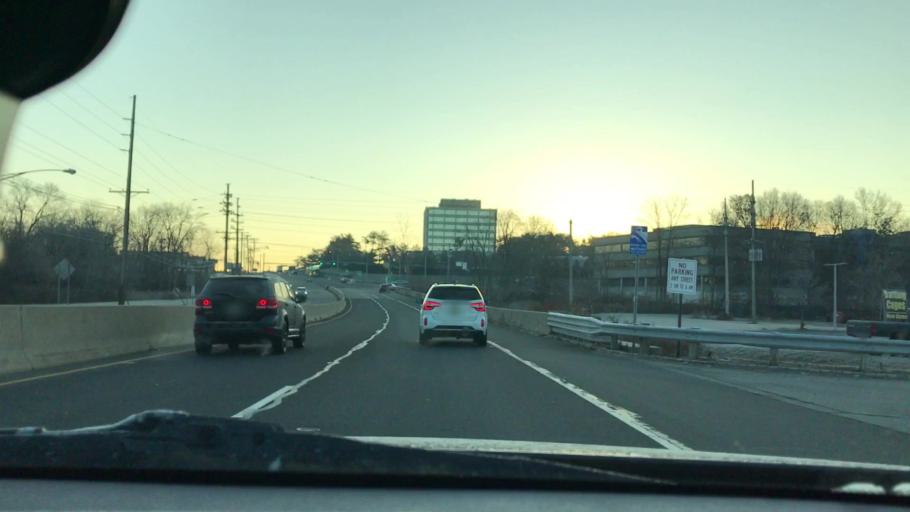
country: US
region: New Jersey
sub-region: Morris County
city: Florham Park
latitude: 40.8132
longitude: -74.3954
